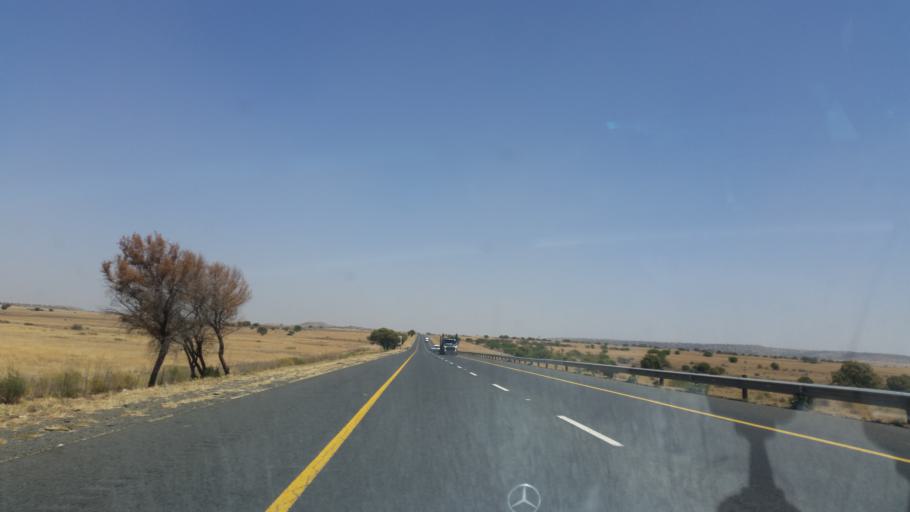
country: ZA
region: Orange Free State
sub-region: Lejweleputswa District Municipality
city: Winburg
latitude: -28.6733
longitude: 26.8412
